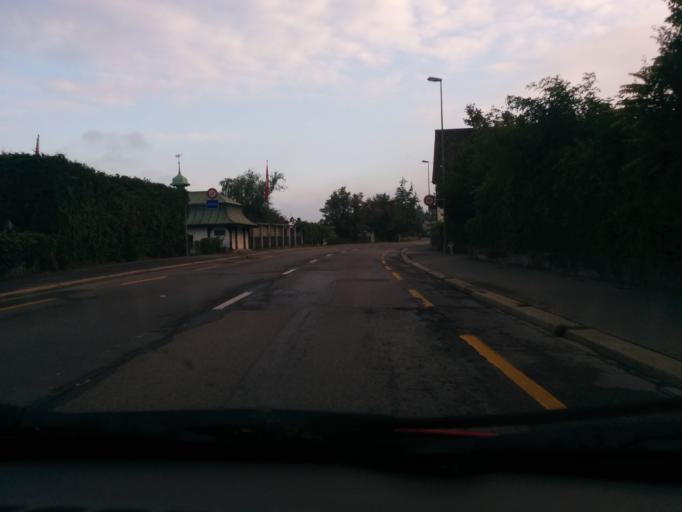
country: CH
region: Zurich
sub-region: Bezirk Meilen
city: Zollikon
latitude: 47.3316
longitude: 8.5720
